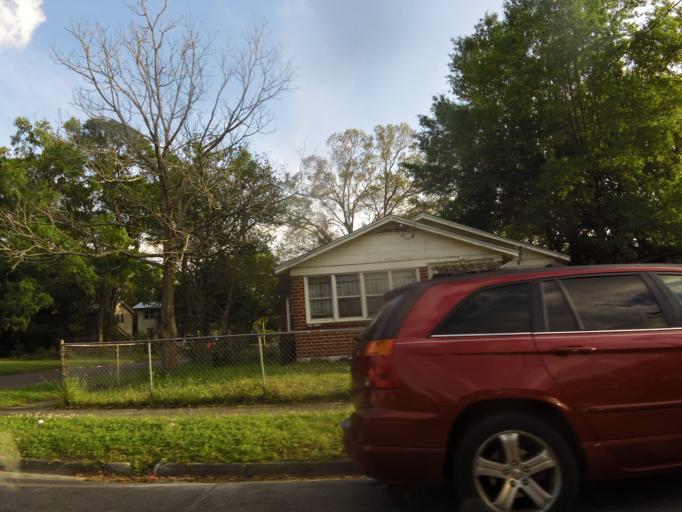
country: US
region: Florida
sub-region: Duval County
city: Jacksonville
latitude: 30.3482
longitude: -81.6775
